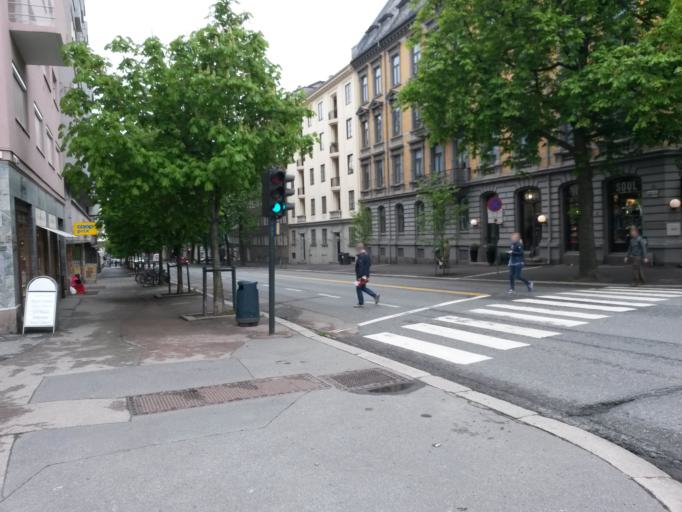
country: NO
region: Oslo
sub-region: Oslo
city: Sjolyststranda
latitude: 59.9173
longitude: 10.7089
